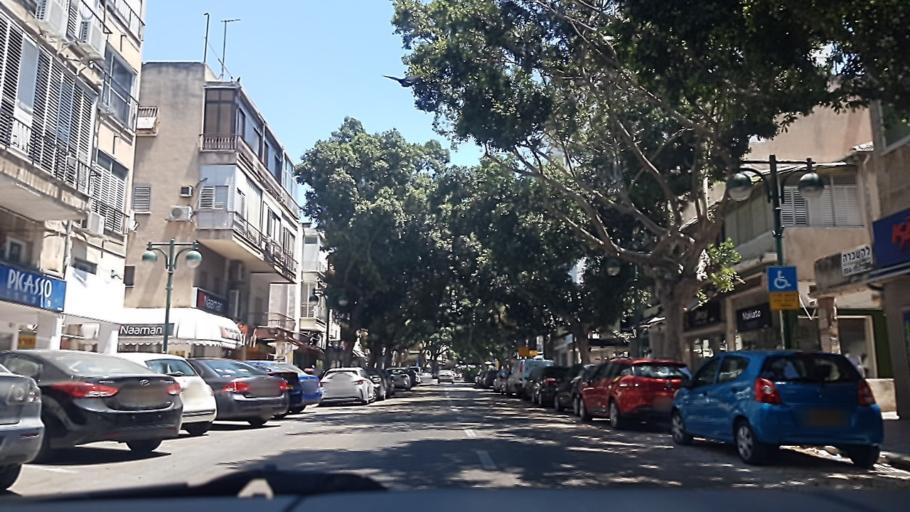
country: IL
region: Tel Aviv
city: Ramat Gan
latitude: 32.0847
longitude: 34.8127
